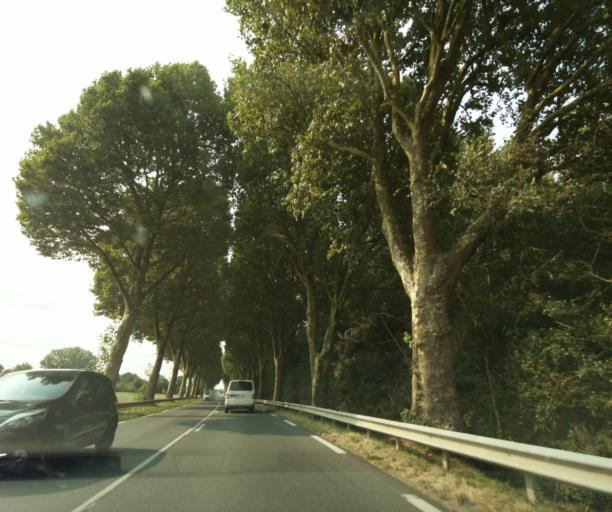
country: FR
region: Centre
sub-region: Departement de l'Indre
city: Chatillon-sur-Indre
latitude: 46.9700
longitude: 1.1963
